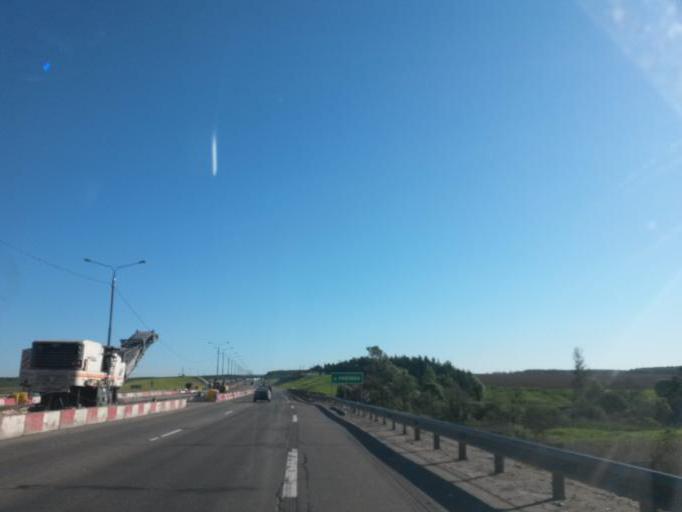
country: RU
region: Moskovskaya
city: Klimovsk
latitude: 55.3472
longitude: 37.5901
